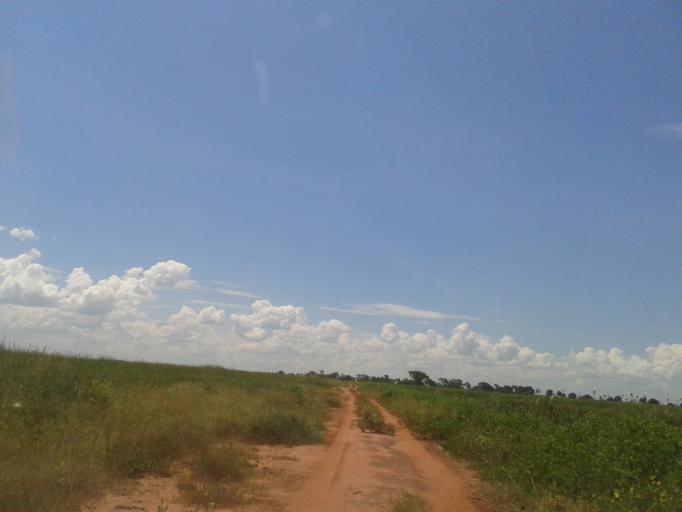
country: BR
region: Minas Gerais
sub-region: Santa Vitoria
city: Santa Vitoria
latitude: -19.1793
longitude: -50.4480
